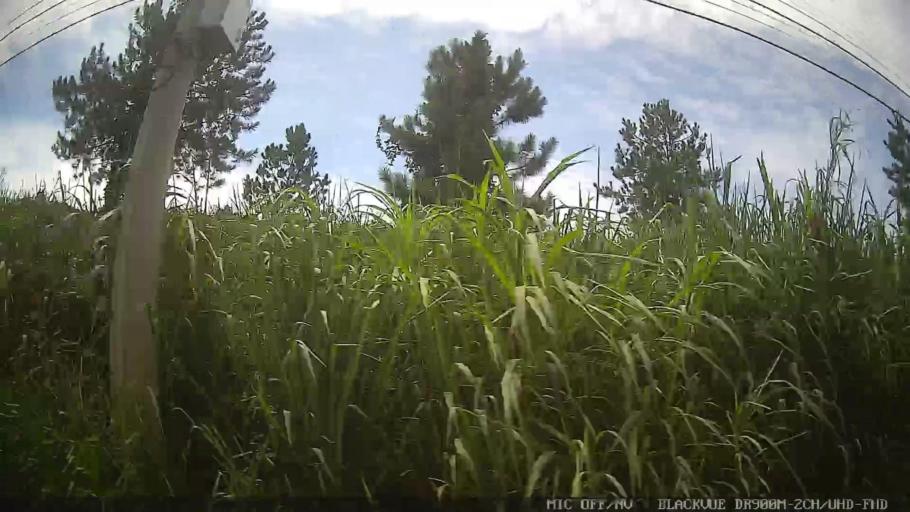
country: BR
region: Sao Paulo
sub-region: Santa Isabel
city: Santa Isabel
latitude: -23.4031
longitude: -46.1991
